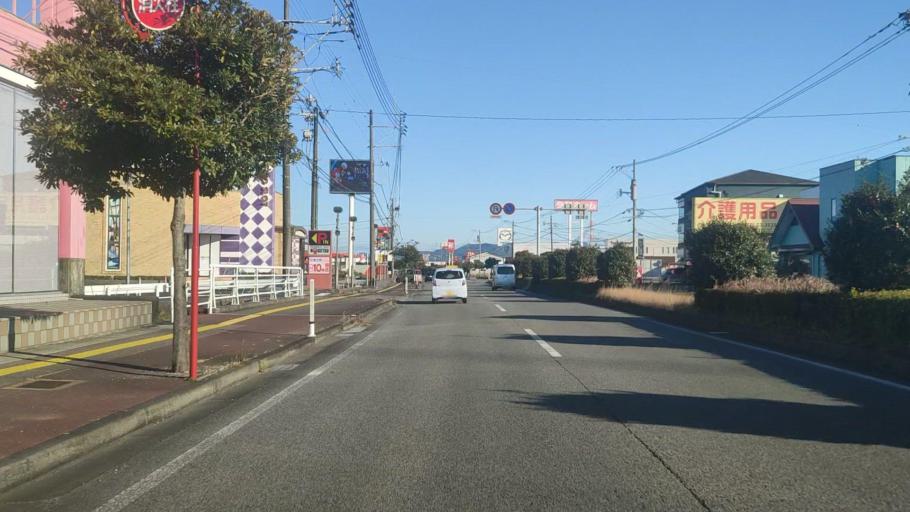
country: JP
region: Miyazaki
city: Nobeoka
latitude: 32.5539
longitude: 131.6790
